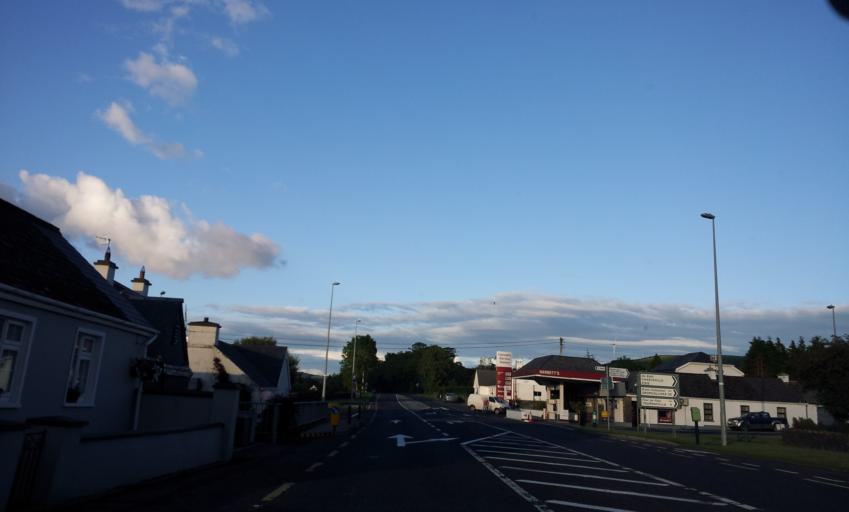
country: IE
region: Munster
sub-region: County Limerick
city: Abbeyfeale
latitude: 52.3825
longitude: -9.2182
